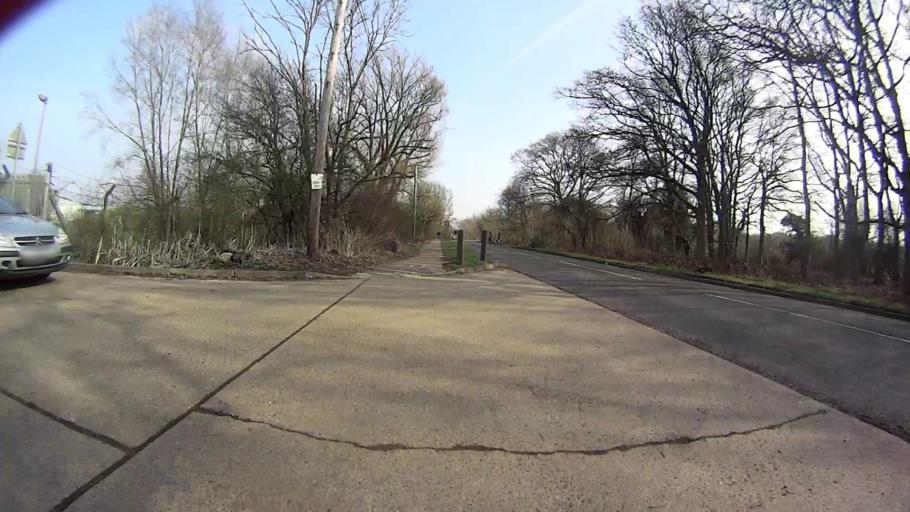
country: GB
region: England
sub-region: Surrey
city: Salfords
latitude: 51.2181
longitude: -0.1782
